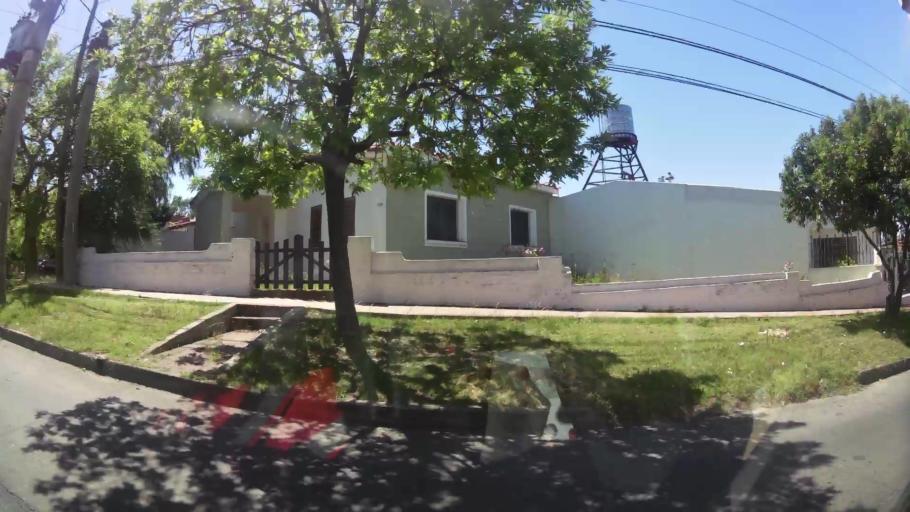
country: AR
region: Cordoba
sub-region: Departamento de Capital
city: Cordoba
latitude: -31.4315
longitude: -64.2115
